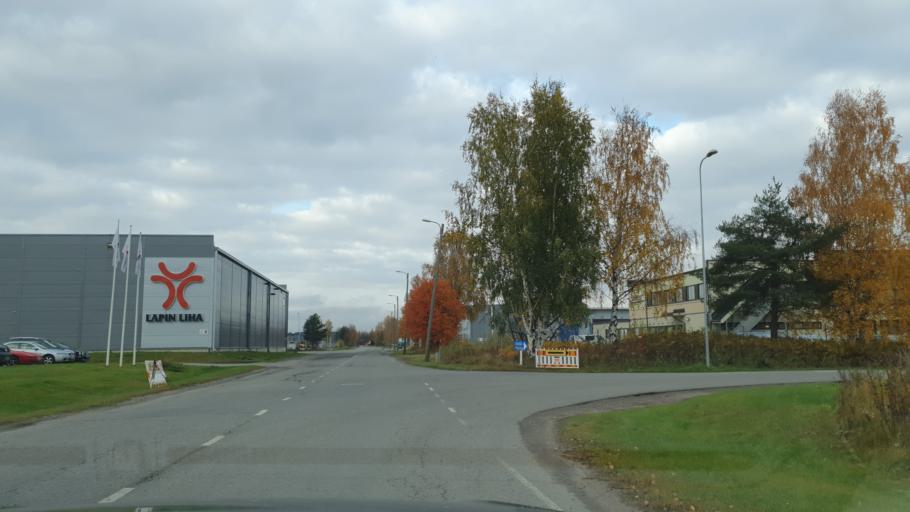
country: FI
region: Lapland
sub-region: Rovaniemi
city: Rovaniemi
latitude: 66.4932
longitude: 25.6656
